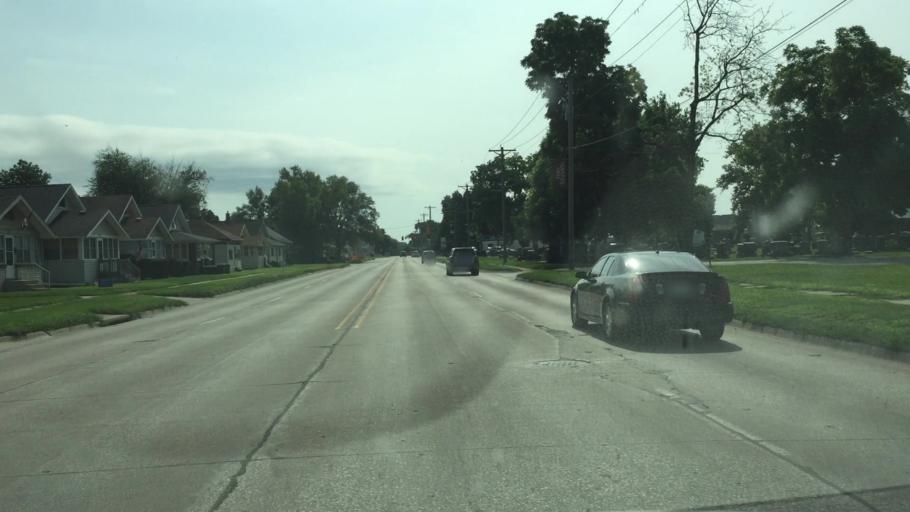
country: US
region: Iowa
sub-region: Lee County
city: Fort Madison
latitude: 40.6272
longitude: -91.3369
